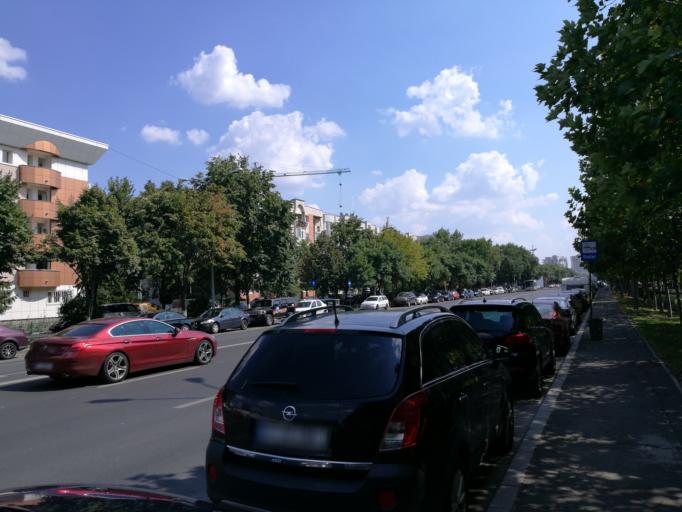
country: RO
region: Bucuresti
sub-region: Municipiul Bucuresti
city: Bucharest
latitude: 44.4861
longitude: 26.0918
